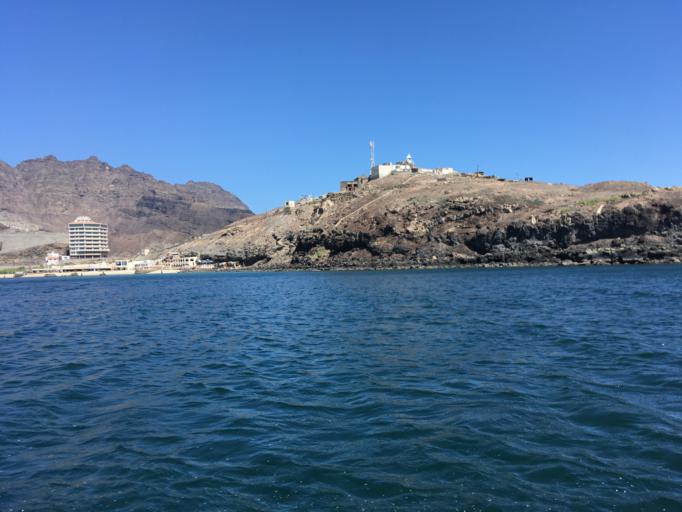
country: YE
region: Aden
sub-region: Attawahi
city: At Tawahi
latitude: 12.7654
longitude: 44.9852
